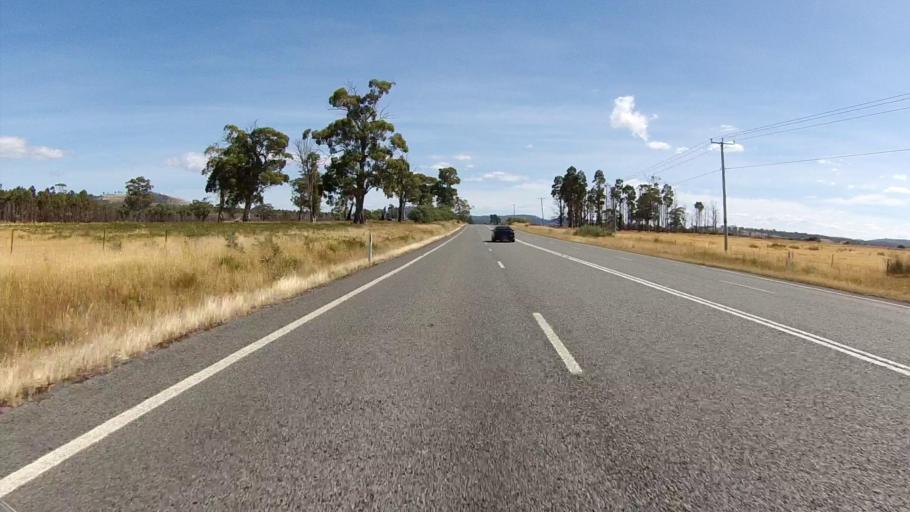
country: AU
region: Tasmania
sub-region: Sorell
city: Sorell
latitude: -42.6004
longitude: 147.7592
